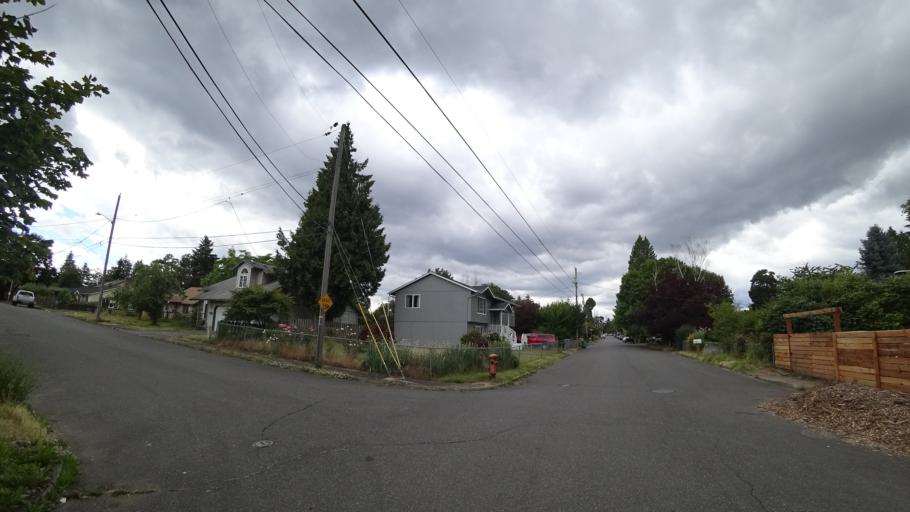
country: US
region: Oregon
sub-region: Multnomah County
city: Portland
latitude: 45.5614
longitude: -122.6152
